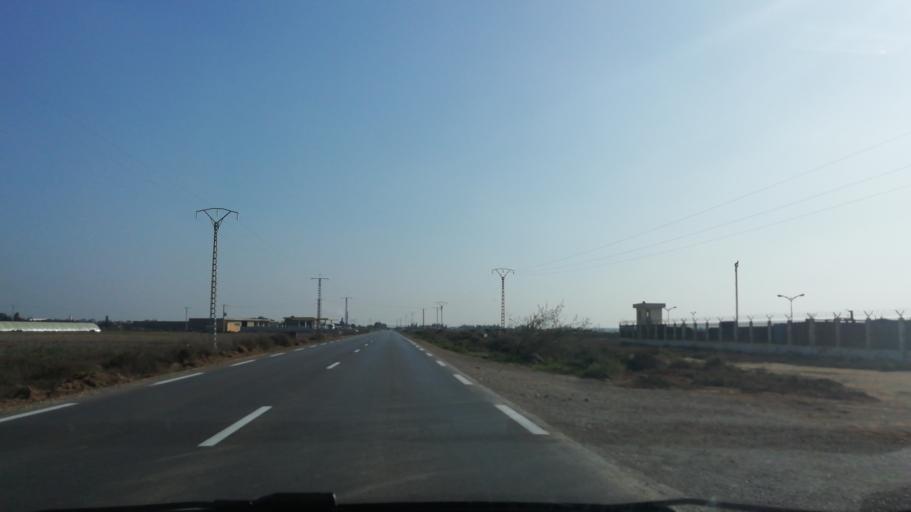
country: DZ
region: Mostaganem
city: Mostaganem
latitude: 35.7487
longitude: 0.0283
